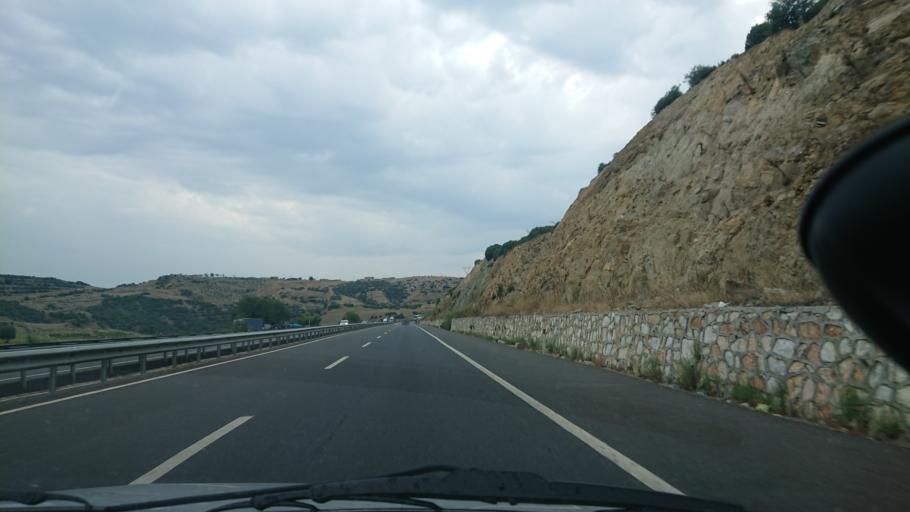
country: TR
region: Manisa
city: Selendi
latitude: 38.6314
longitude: 28.9468
